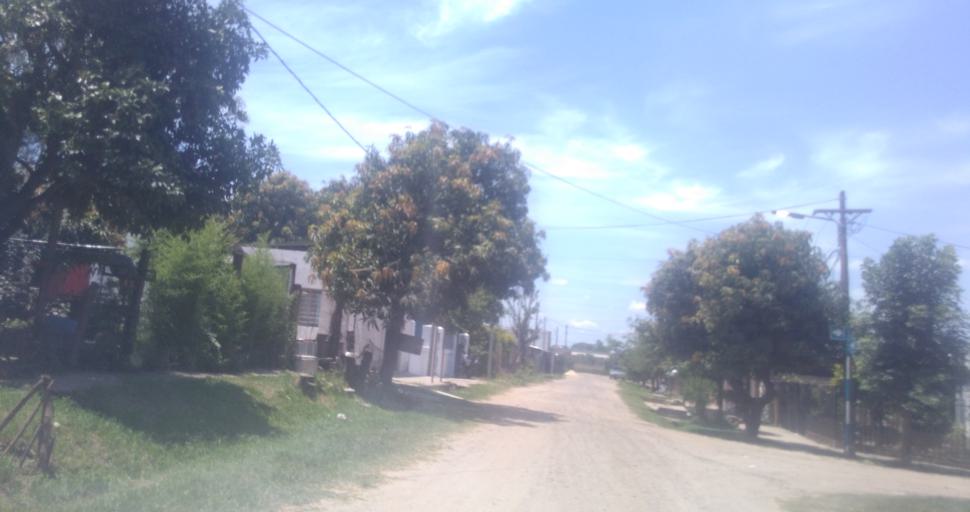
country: AR
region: Chaco
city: Fontana
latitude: -27.4160
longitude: -59.0281
